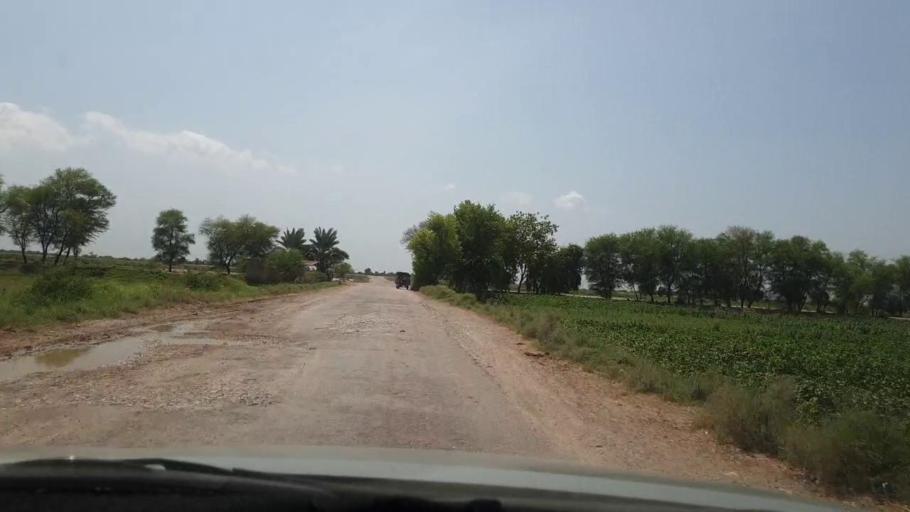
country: PK
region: Sindh
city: Rohri
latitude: 27.6695
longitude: 69.0545
